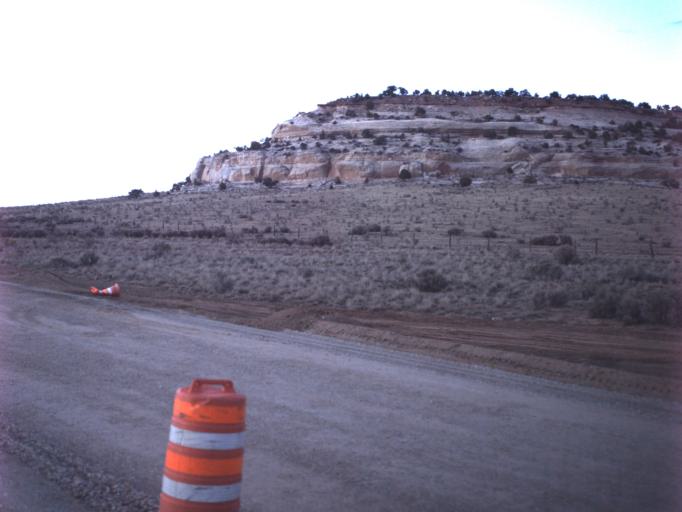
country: US
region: Utah
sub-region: San Juan County
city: Monticello
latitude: 38.0974
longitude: -109.3593
